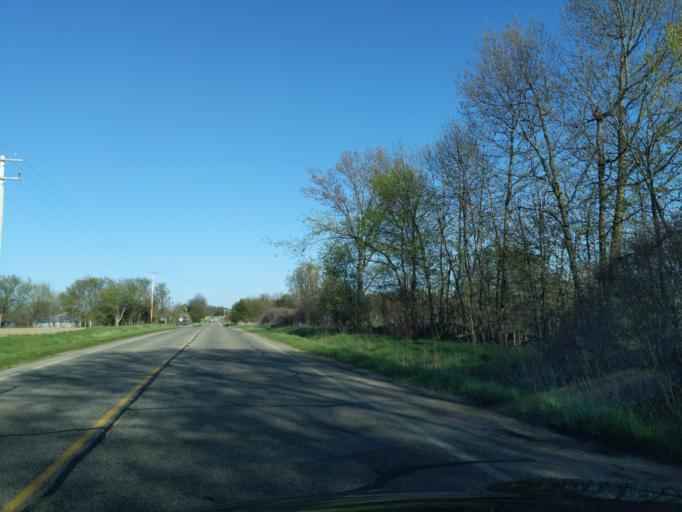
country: US
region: Michigan
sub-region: Ionia County
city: Portland
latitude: 42.8816
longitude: -84.9828
